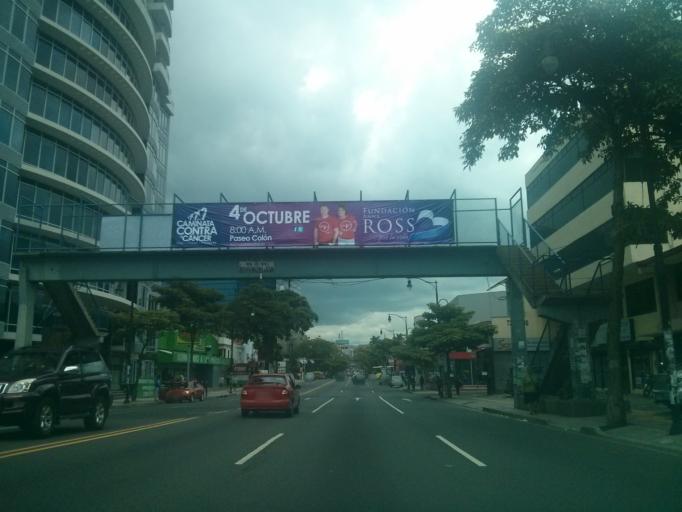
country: CR
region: San Jose
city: San Jose
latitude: 9.9352
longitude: -84.0914
